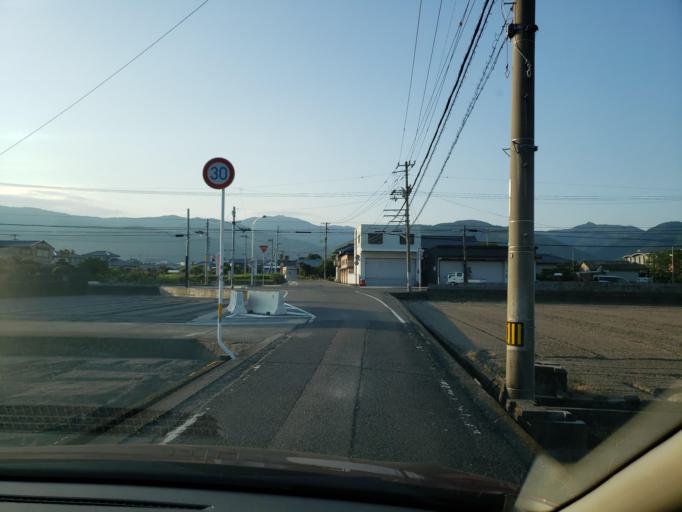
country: JP
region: Tokushima
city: Wakimachi
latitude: 34.0829
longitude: 134.2335
